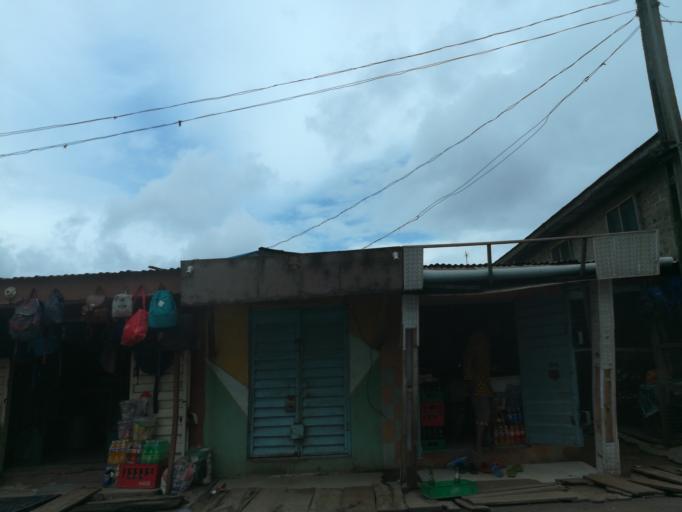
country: NG
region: Lagos
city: Agege
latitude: 6.6113
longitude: 3.3175
